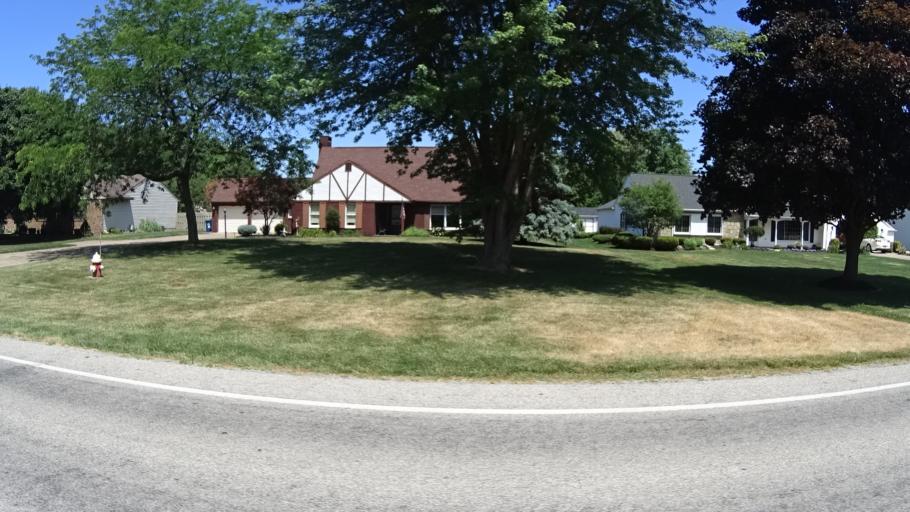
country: US
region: Ohio
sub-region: Erie County
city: Sandusky
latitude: 41.3963
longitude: -82.6893
